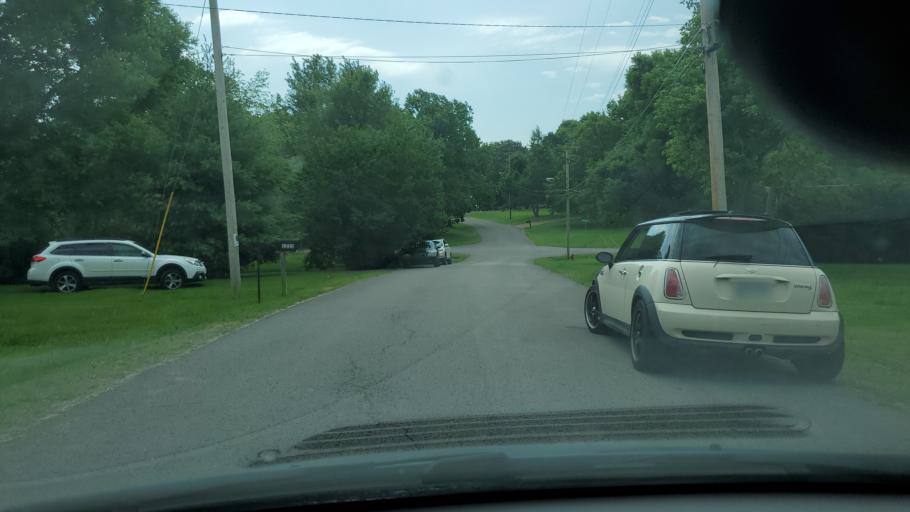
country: US
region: Tennessee
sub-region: Davidson County
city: Lakewood
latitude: 36.2251
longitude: -86.7194
